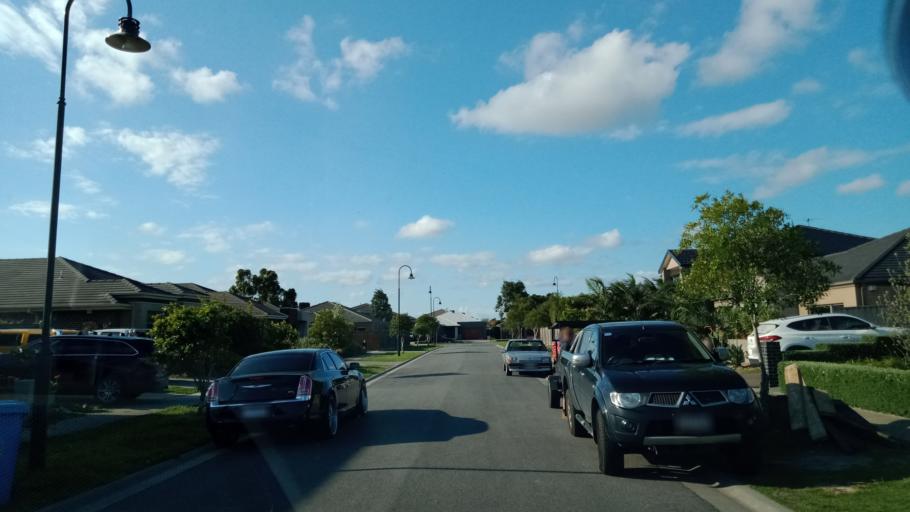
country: AU
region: Victoria
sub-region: Casey
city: Lynbrook
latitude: -38.0771
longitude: 145.2456
